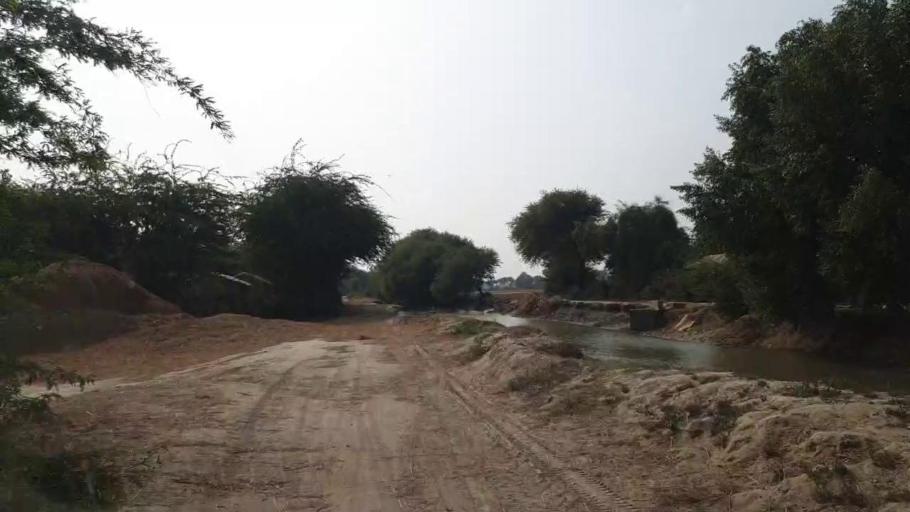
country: PK
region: Sindh
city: Kario
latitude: 24.7810
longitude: 68.5637
